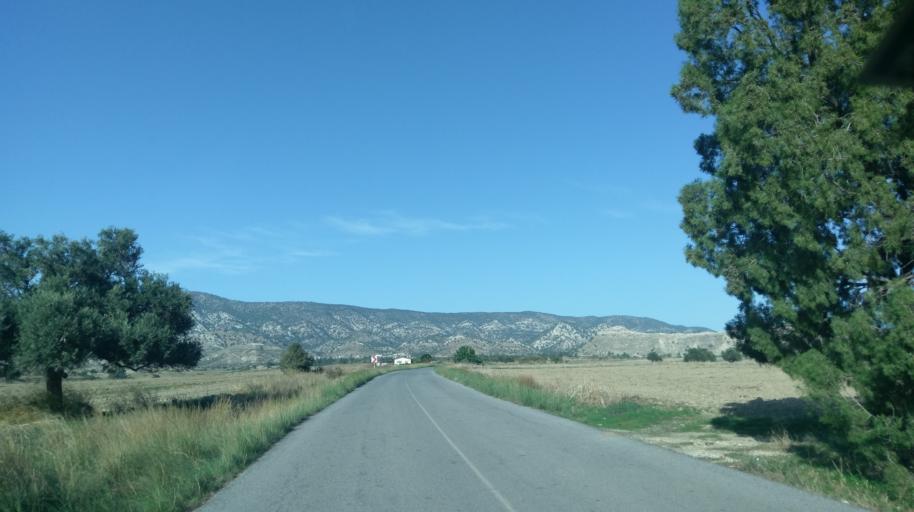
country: CY
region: Ammochostos
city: Lefkonoiko
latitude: 35.3103
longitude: 33.7485
